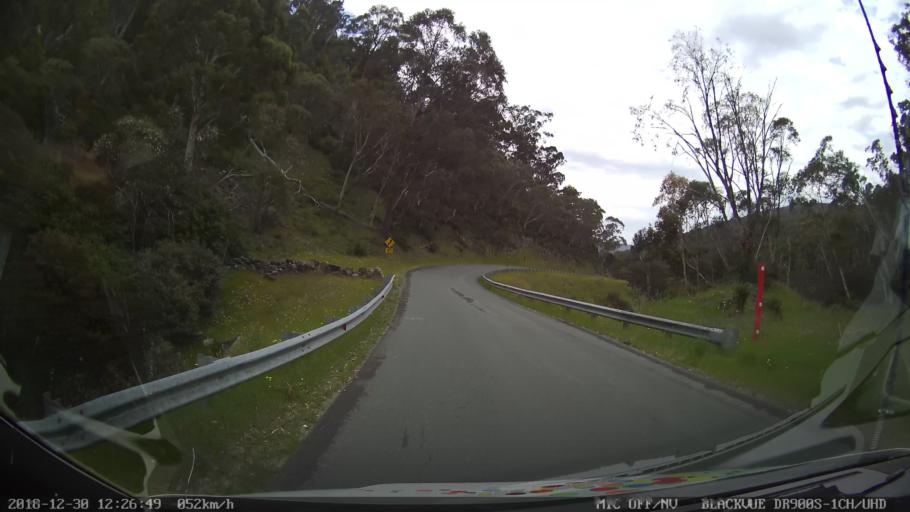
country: AU
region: New South Wales
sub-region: Snowy River
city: Jindabyne
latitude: -36.3354
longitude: 148.4897
